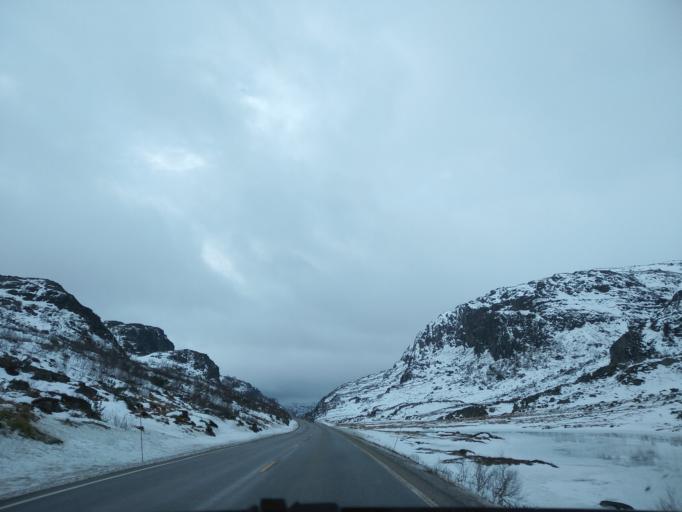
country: NO
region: Vest-Agder
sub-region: Sirdal
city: Tonstad
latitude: 58.9043
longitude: 6.7051
